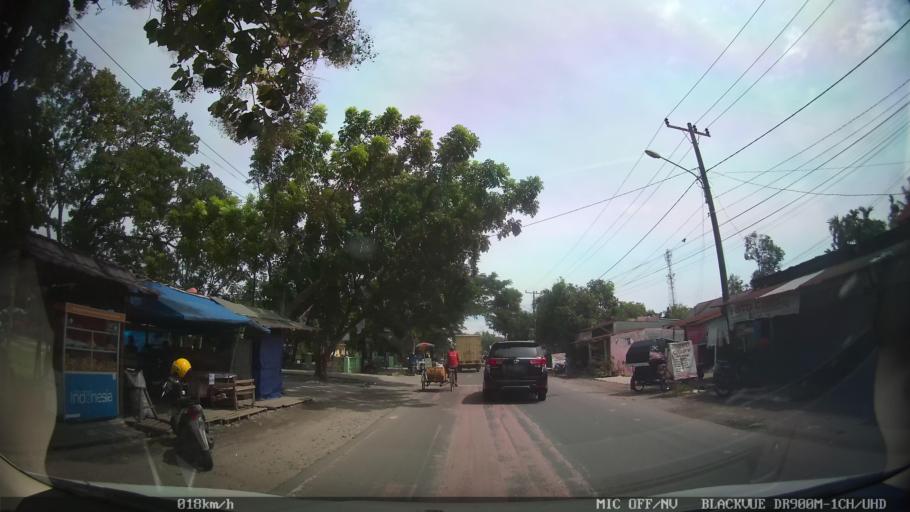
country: ID
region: North Sumatra
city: Medan
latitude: 3.6338
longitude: 98.7163
